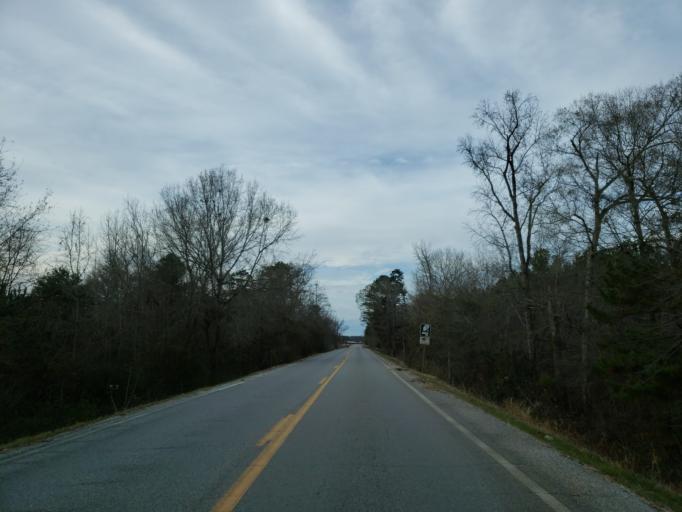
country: US
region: Mississippi
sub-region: Clarke County
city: Quitman
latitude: 31.8733
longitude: -88.7054
